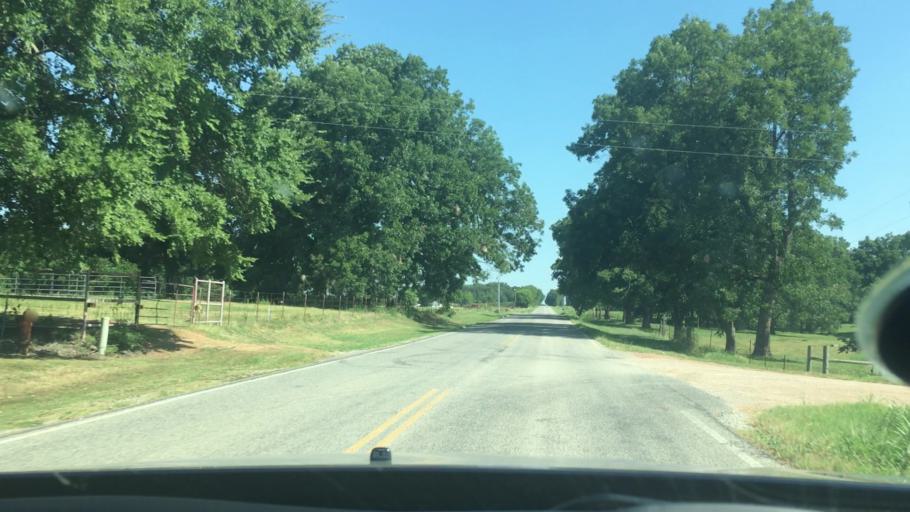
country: US
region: Oklahoma
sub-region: Johnston County
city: Tishomingo
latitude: 34.2884
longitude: -96.6185
